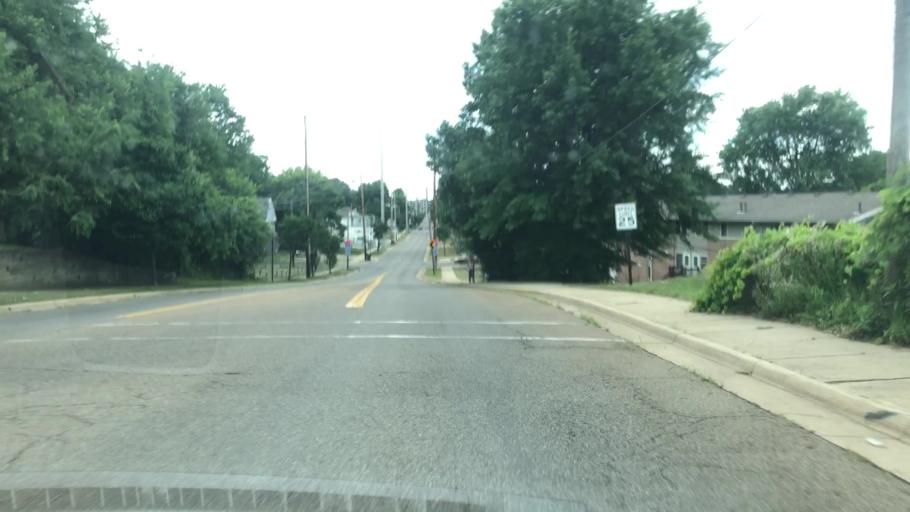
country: US
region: Ohio
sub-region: Summit County
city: Akron
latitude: 41.0575
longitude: -81.5413
